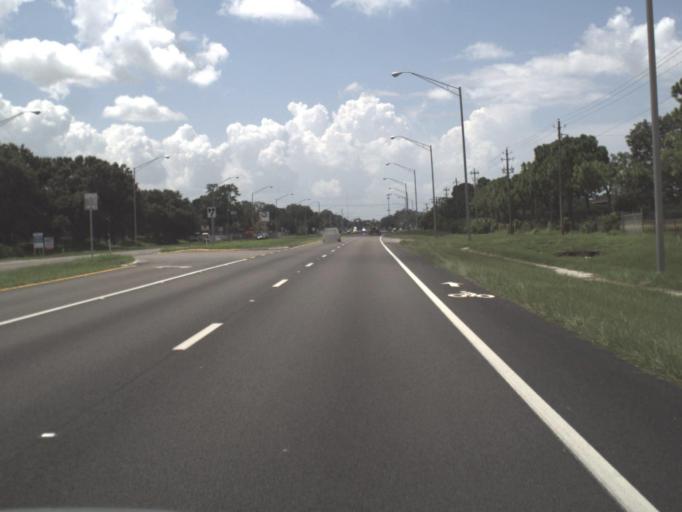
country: US
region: Florida
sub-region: Hillsborough County
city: East Lake-Orient Park
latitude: 27.9878
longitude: -82.3592
